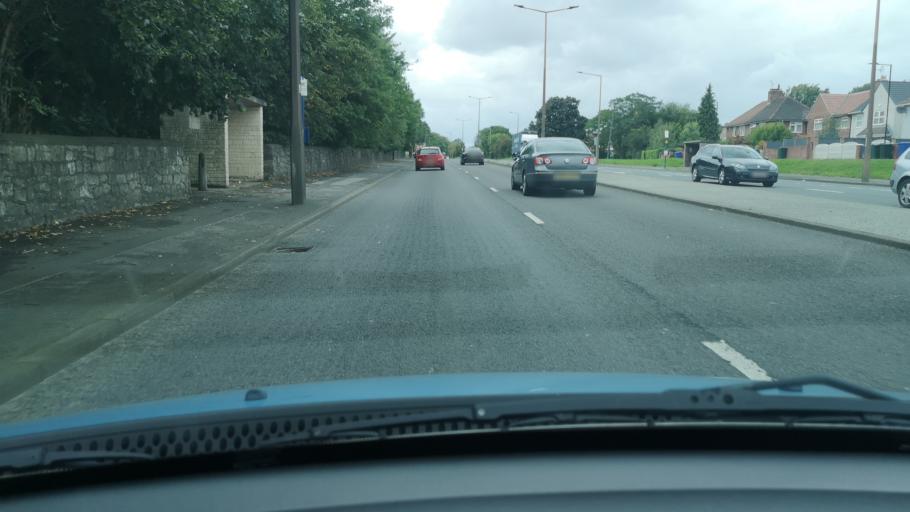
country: GB
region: England
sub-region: Doncaster
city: Carcroft
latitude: 53.5579
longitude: -1.1832
